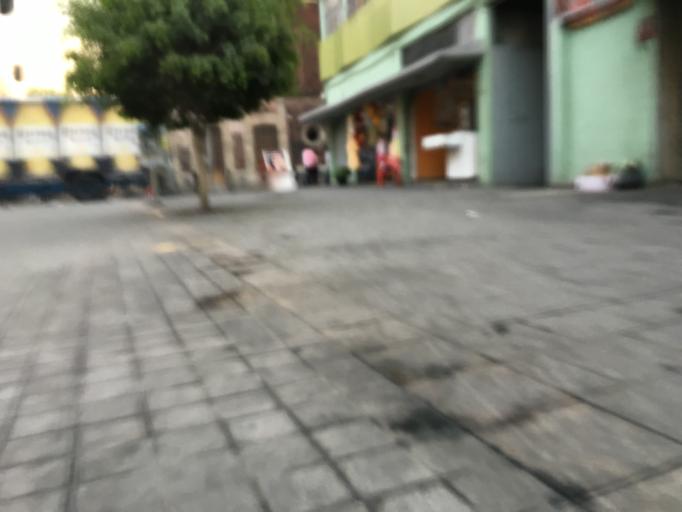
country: MX
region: Mexico City
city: Mexico City
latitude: 19.4286
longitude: -99.1270
